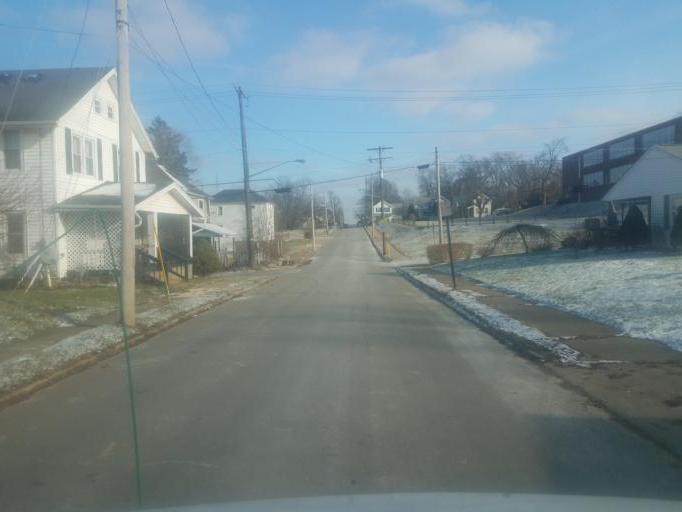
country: US
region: Ohio
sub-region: Richland County
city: Mansfield
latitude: 40.7542
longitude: -82.5117
